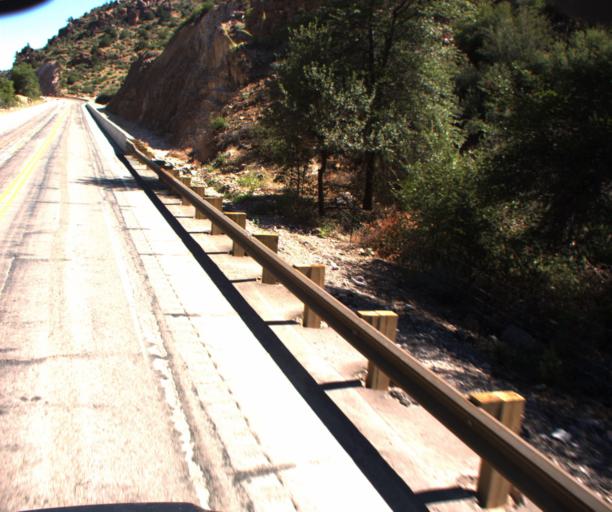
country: US
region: Arizona
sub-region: Pinal County
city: Superior
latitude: 33.3259
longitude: -111.0323
